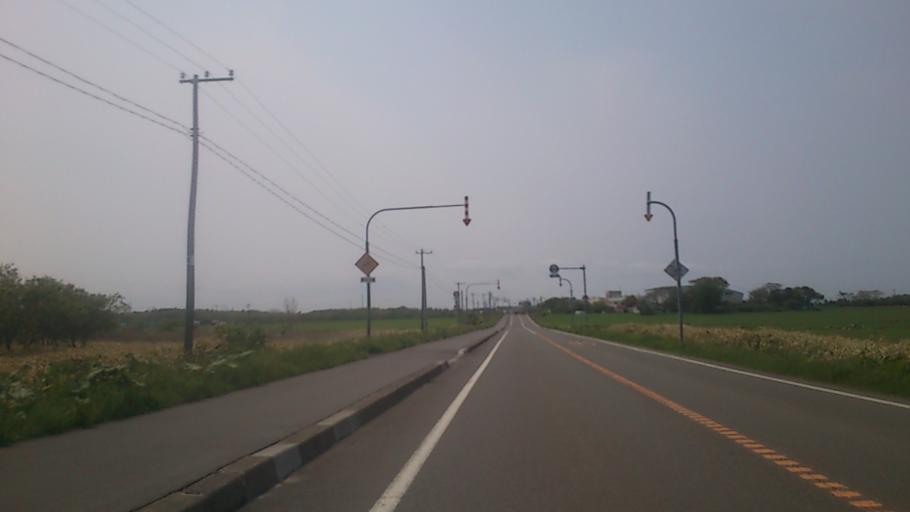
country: JP
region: Hokkaido
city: Nemuro
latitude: 43.2772
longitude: 145.5242
